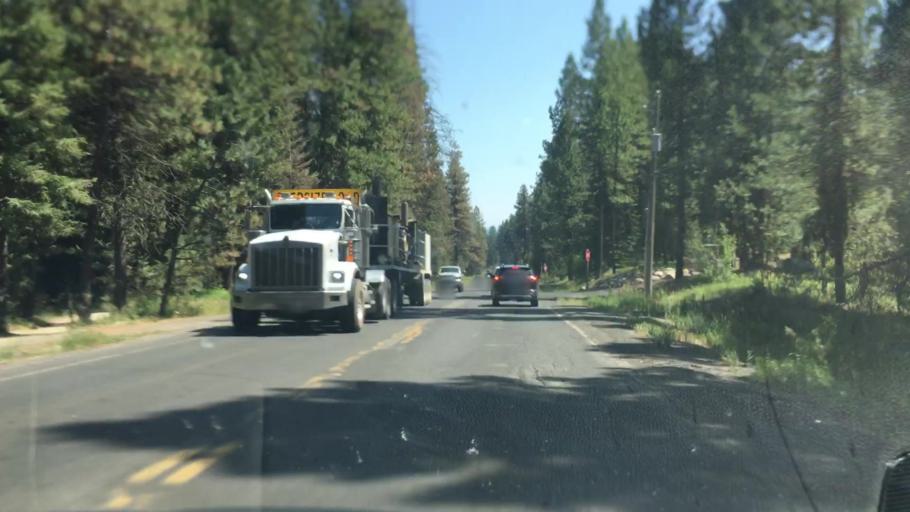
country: US
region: Idaho
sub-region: Valley County
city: McCall
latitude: 44.9206
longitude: -116.1376
